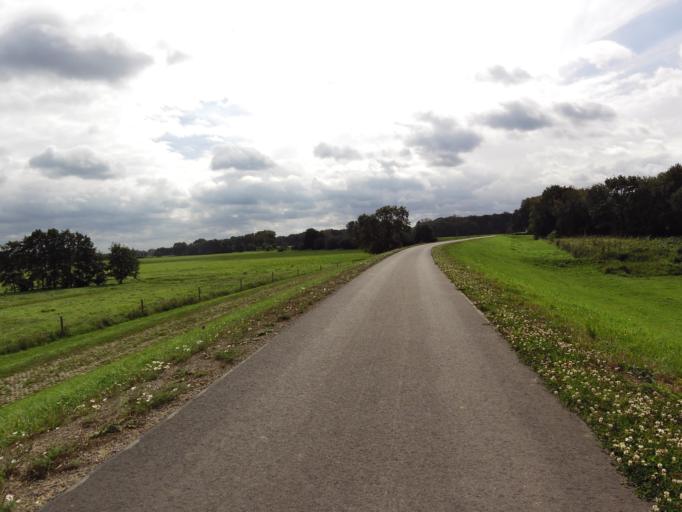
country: DE
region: Saxony-Anhalt
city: Havelberg
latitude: 52.8411
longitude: 12.0465
